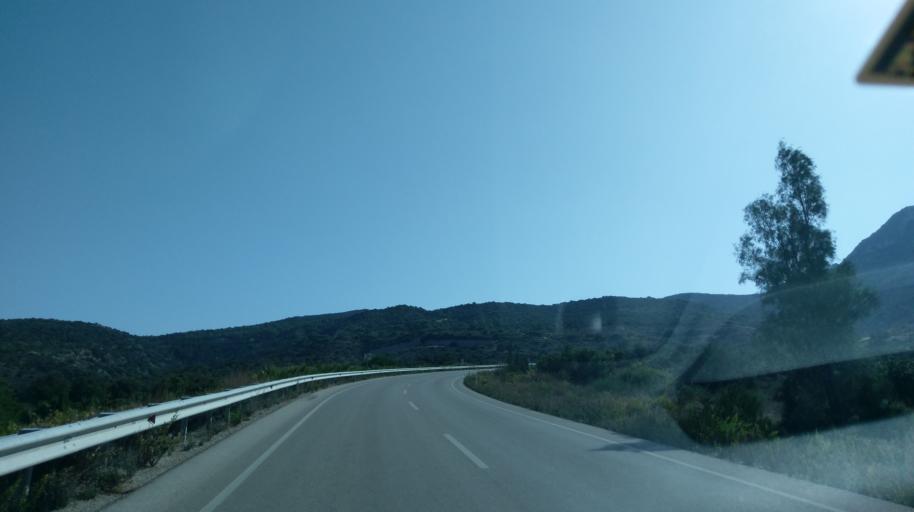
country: CY
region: Ammochostos
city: Trikomo
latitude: 35.4357
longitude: 33.9608
